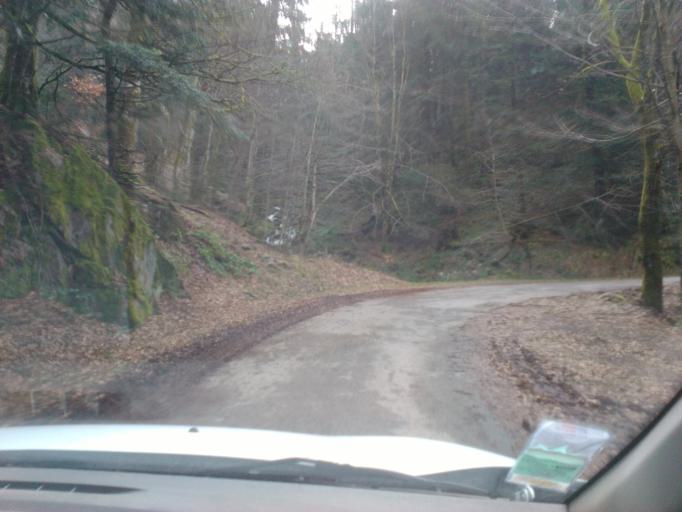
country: FR
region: Lorraine
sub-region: Departement des Vosges
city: Bussang
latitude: 47.8733
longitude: 6.8584
